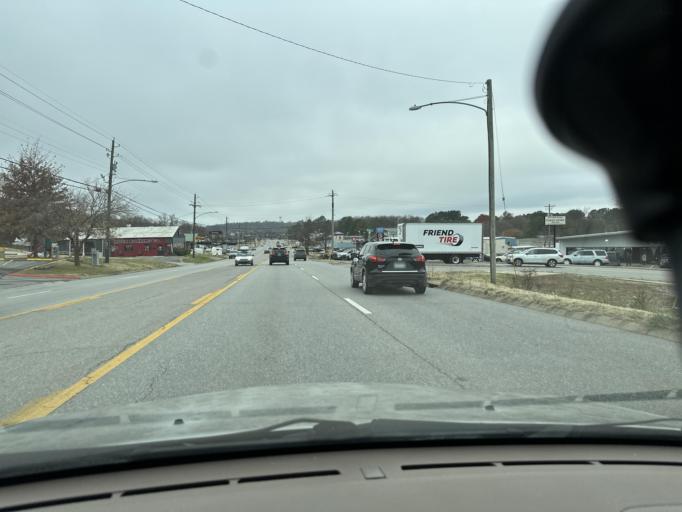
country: US
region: Arkansas
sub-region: Washington County
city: Johnson
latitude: 36.0998
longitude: -94.1502
